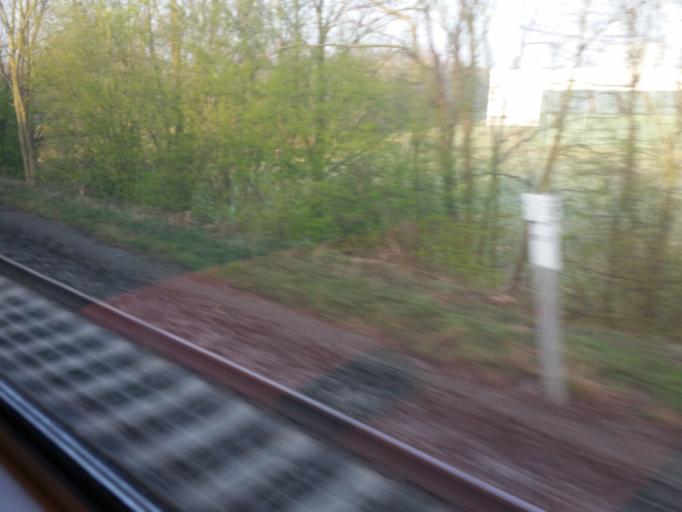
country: BE
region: Flanders
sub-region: Provincie Vlaams-Brabant
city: Vilvoorde
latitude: 50.9417
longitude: 4.4449
